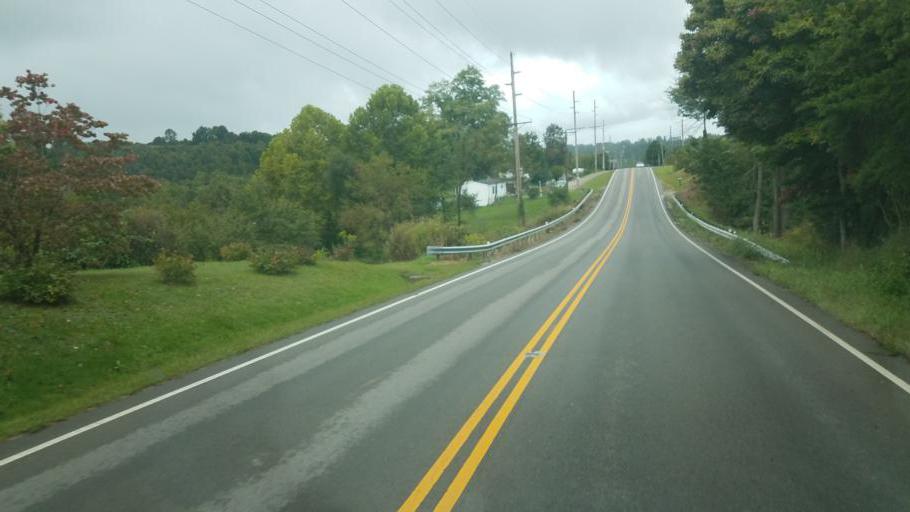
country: US
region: Ohio
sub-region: Scioto County
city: Wheelersburg
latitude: 38.7697
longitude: -82.7925
